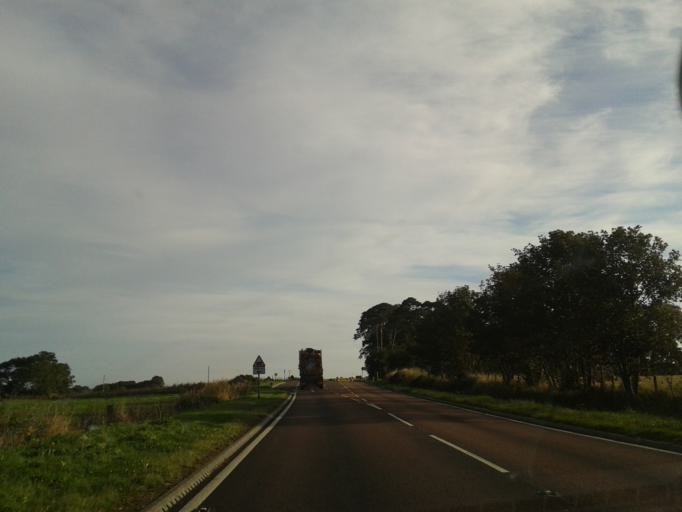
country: GB
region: Scotland
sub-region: Highland
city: Inverness
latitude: 57.4985
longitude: -4.1471
